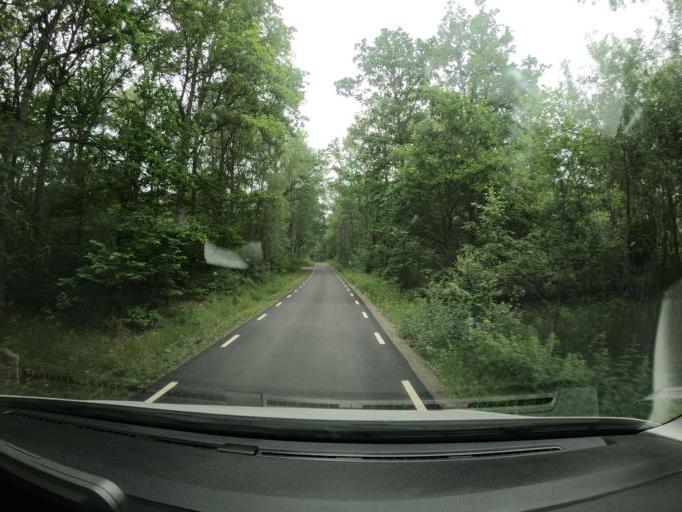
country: SE
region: Skane
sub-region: Perstorps Kommun
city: Perstorp
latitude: 56.0242
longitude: 13.3468
